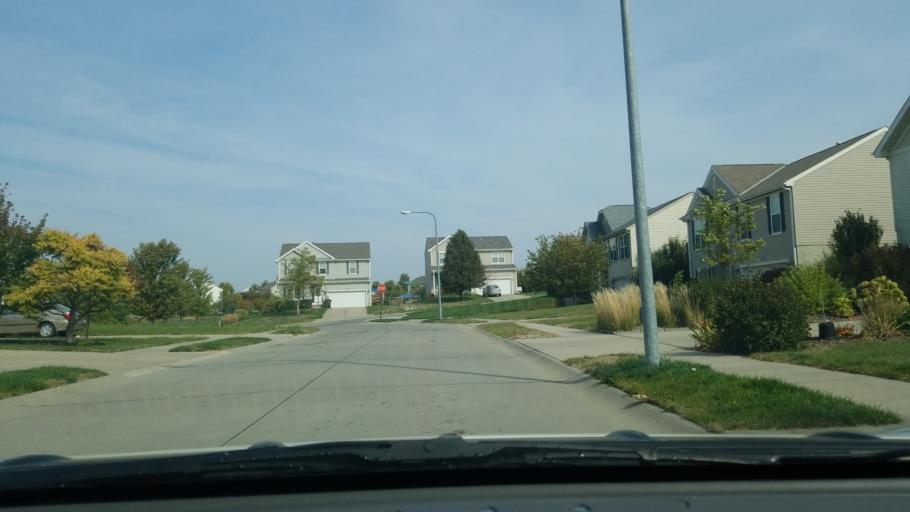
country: US
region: Nebraska
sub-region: Sarpy County
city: Papillion
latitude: 41.1278
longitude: -96.0578
